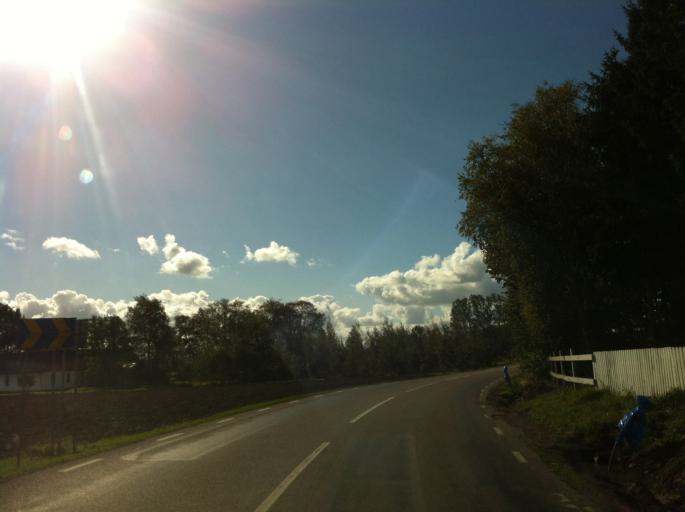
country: SE
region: Skane
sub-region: Sjobo Kommun
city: Sjoebo
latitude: 55.6495
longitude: 13.8082
